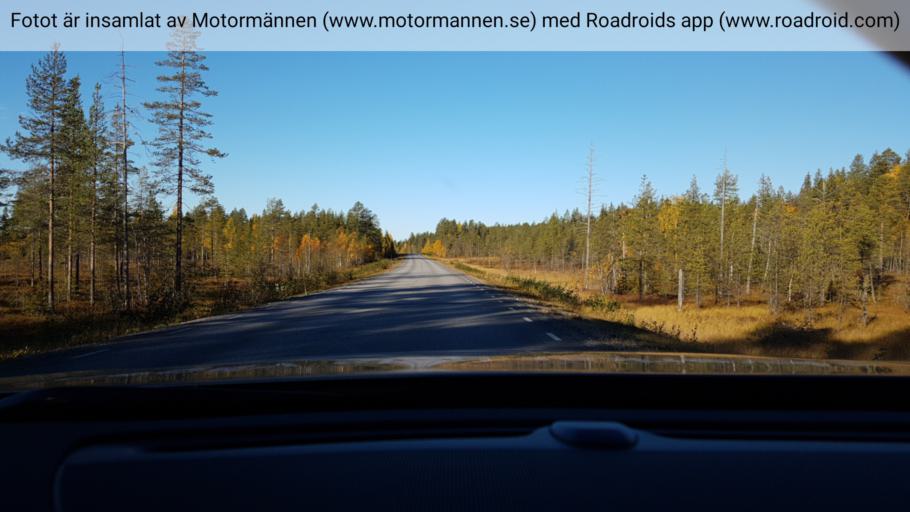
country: SE
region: Vaesterbotten
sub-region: Skelleftea Kommun
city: Storvik
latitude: 65.3288
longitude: 20.6565
